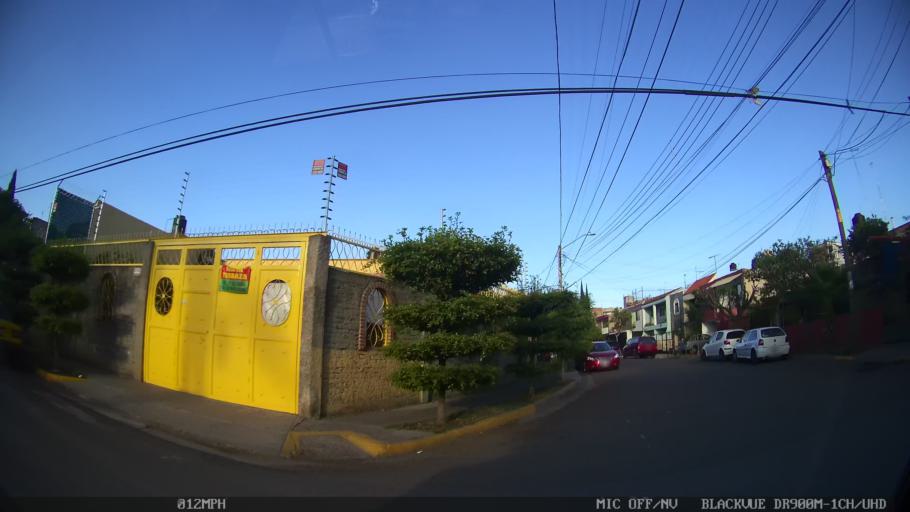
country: MX
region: Jalisco
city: Tlaquepaque
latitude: 20.7112
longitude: -103.2997
